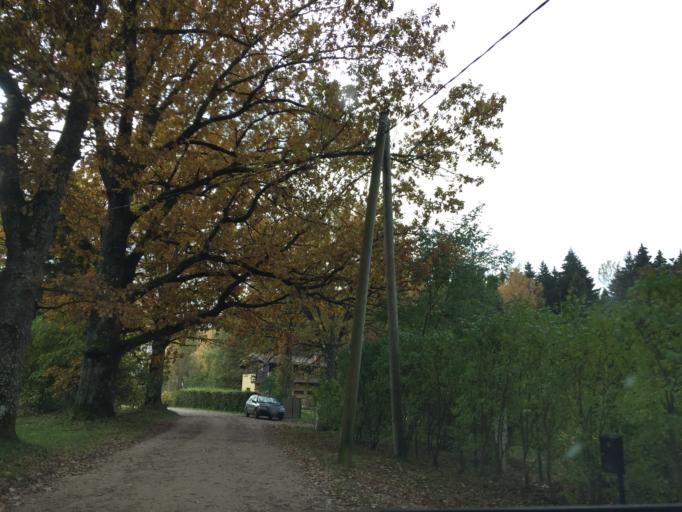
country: LV
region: Lielvarde
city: Lielvarde
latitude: 56.7302
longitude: 24.7862
